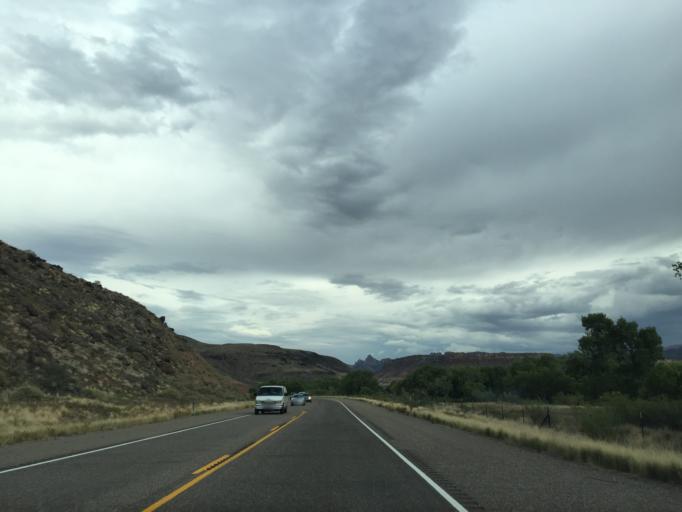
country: US
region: Utah
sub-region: Washington County
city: LaVerkin
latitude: 37.1808
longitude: -113.1285
